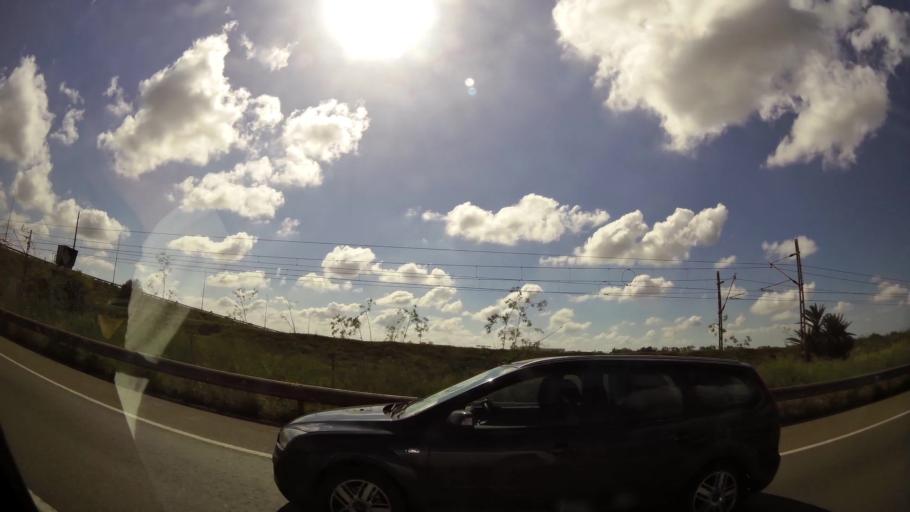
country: MA
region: Grand Casablanca
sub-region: Nouaceur
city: Bouskoura
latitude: 33.4242
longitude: -7.6274
